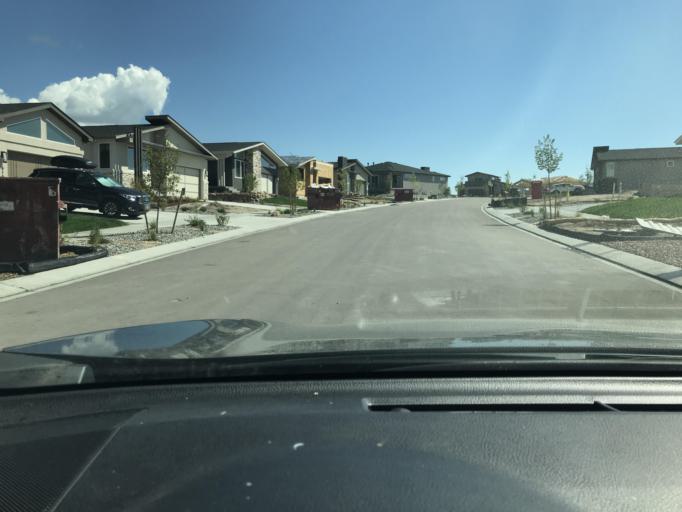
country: US
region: Colorado
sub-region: El Paso County
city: Black Forest
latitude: 38.9655
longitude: -104.7094
